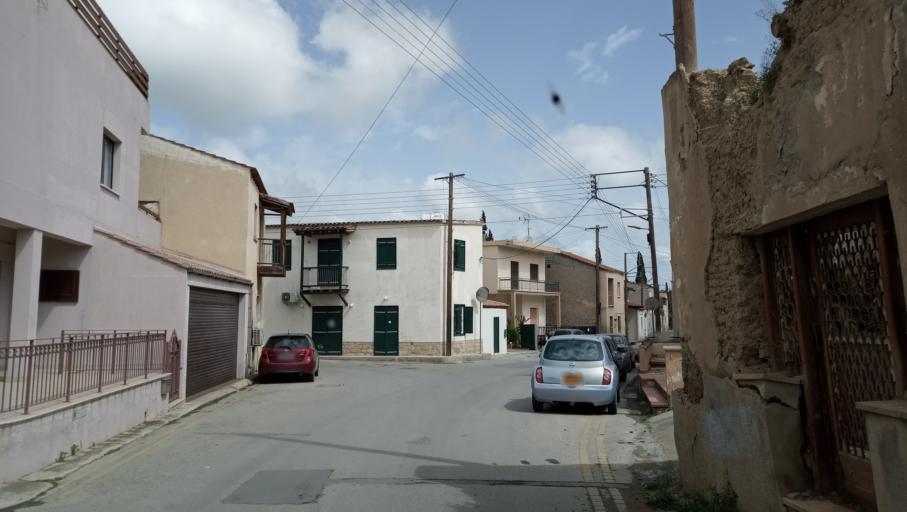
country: CY
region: Lefkosia
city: Dali
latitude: 35.0258
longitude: 33.4234
